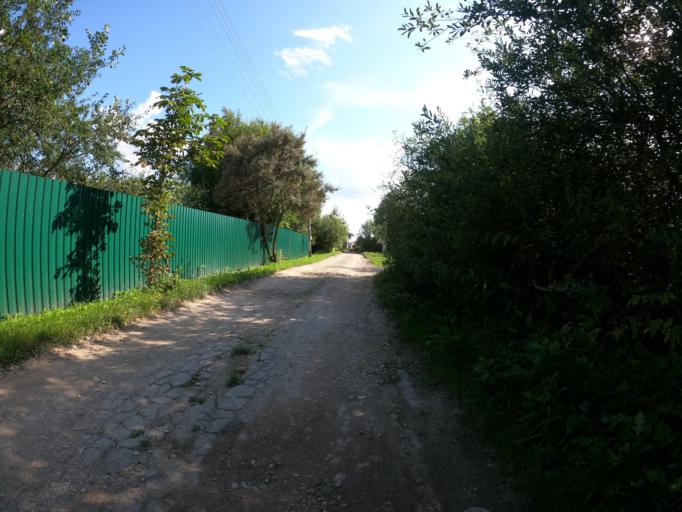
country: RU
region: Moskovskaya
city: Troitskoye
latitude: 55.2346
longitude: 38.4893
